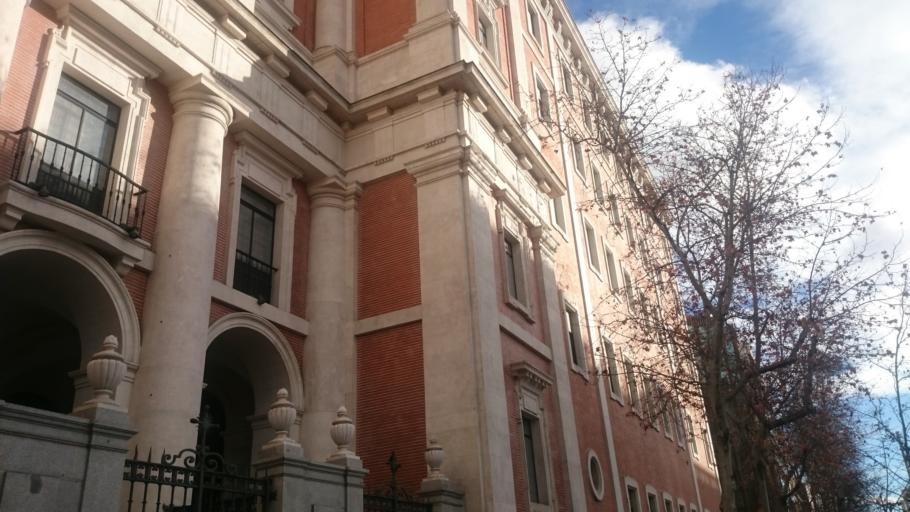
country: ES
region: Madrid
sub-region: Provincia de Madrid
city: Salamanca
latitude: 40.4346
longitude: -3.6864
